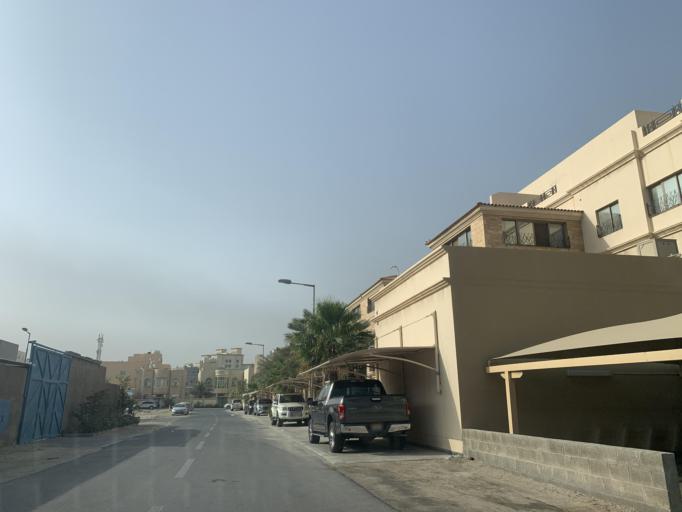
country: BH
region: Northern
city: Madinat `Isa
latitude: 26.1898
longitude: 50.5582
